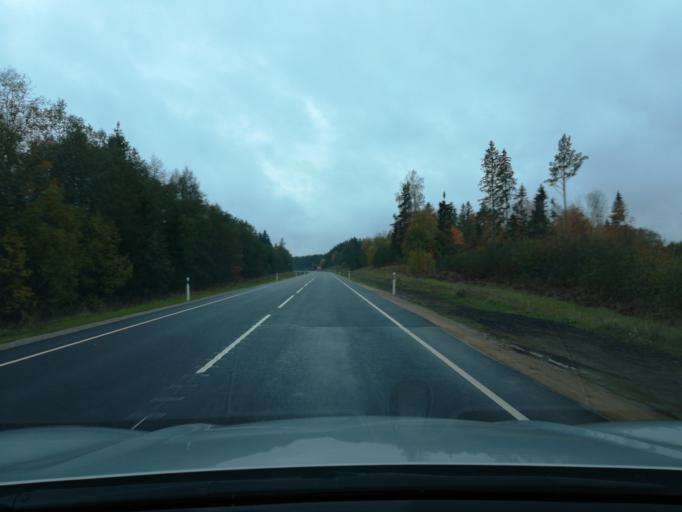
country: EE
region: Ida-Virumaa
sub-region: Johvi vald
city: Johvi
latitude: 59.1367
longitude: 27.3438
